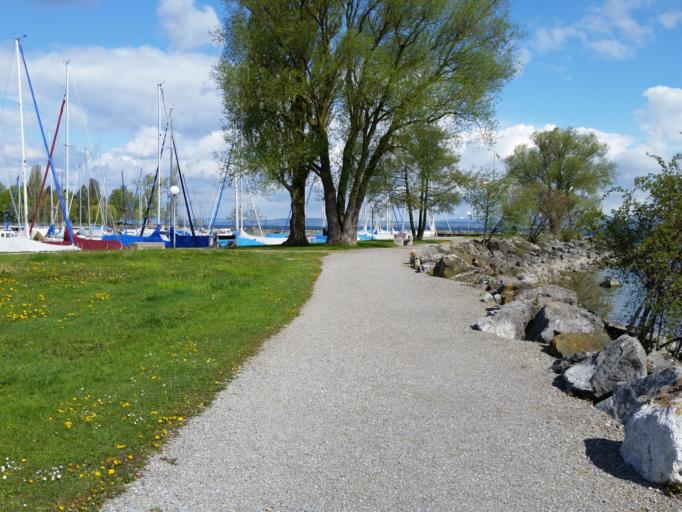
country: CH
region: Thurgau
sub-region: Arbon District
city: Romanshorn
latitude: 47.5688
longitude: 9.3853
